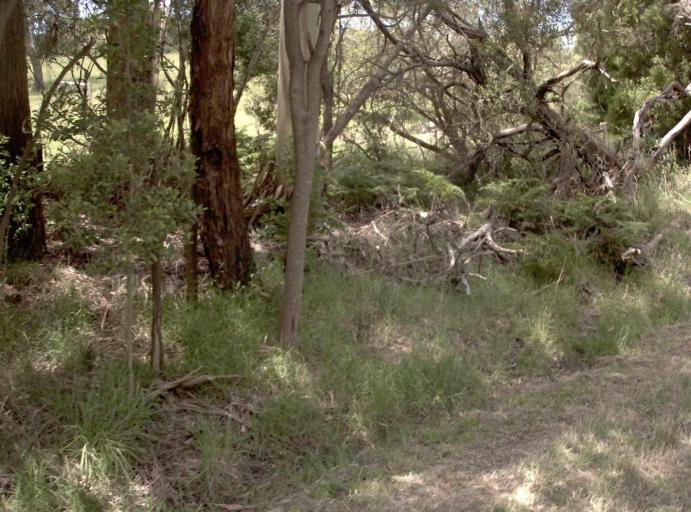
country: AU
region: Victoria
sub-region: Bass Coast
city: North Wonthaggi
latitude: -38.7248
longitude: 146.1212
